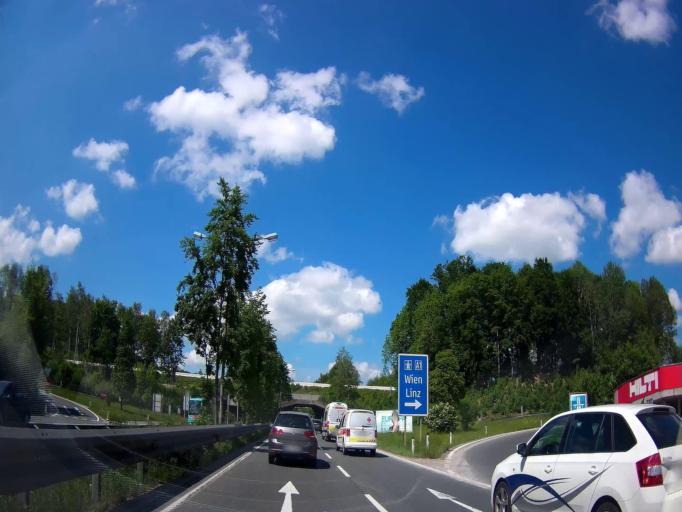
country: AT
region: Salzburg
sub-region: Politischer Bezirk Salzburg-Umgebung
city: Bergheim
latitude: 47.8296
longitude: 13.0569
